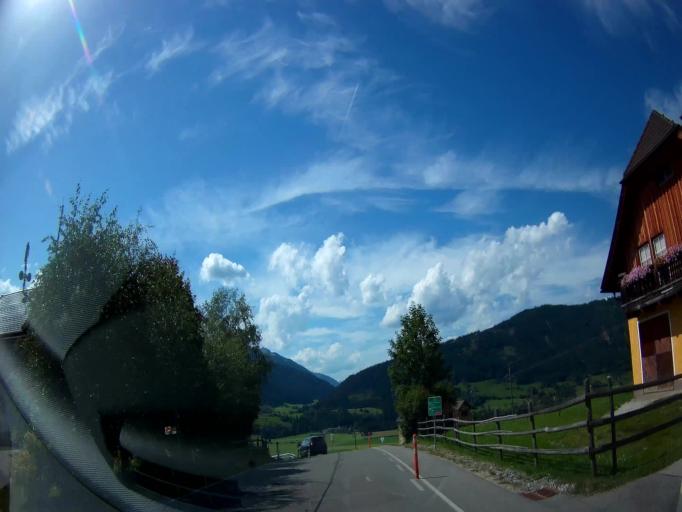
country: AT
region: Salzburg
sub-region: Politischer Bezirk Tamsweg
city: Thomatal
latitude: 47.0839
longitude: 13.7205
